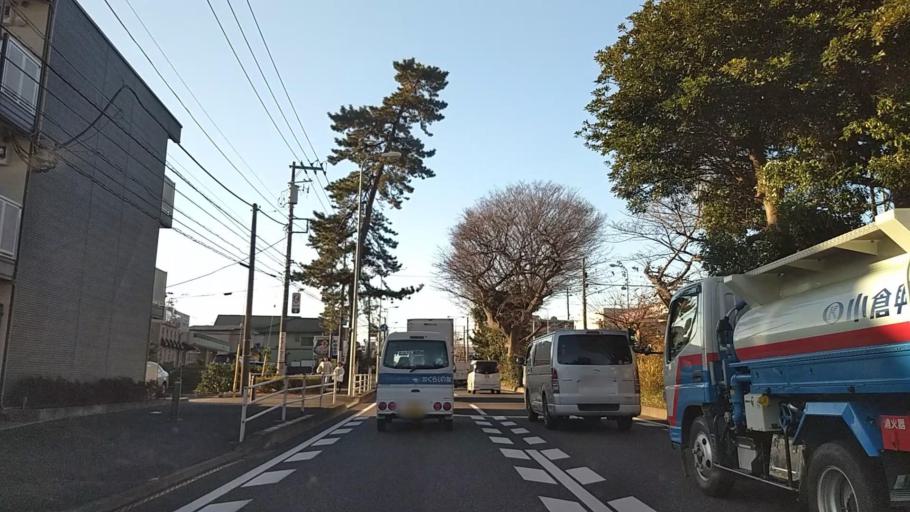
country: JP
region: Kanagawa
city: Fujisawa
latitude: 35.3714
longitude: 139.5016
